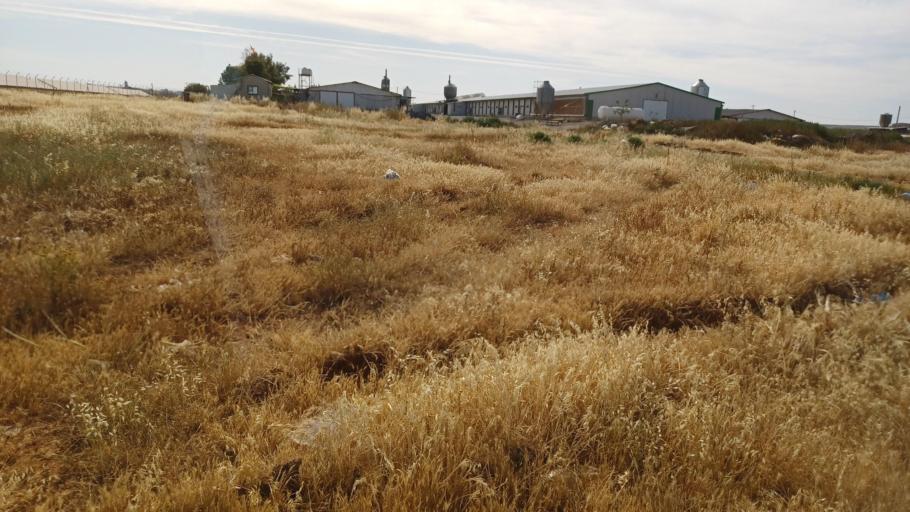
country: CY
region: Lefkosia
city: Kokkinotrimithia
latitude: 35.1643
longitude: 33.1780
